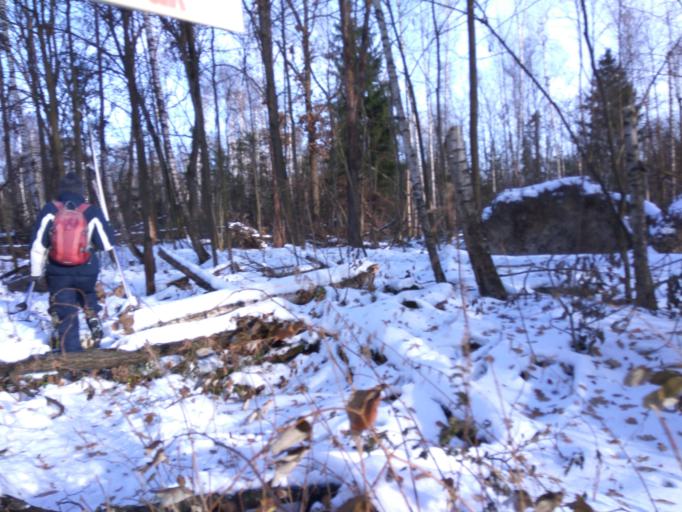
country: RU
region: Moskovskaya
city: Bogorodskoye
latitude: 55.8372
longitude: 37.7103
